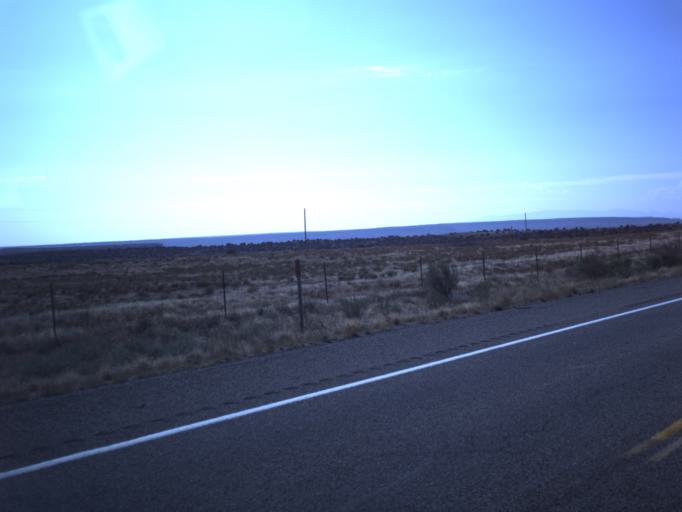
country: US
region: Utah
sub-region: San Juan County
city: Blanding
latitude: 37.4482
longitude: -109.4671
